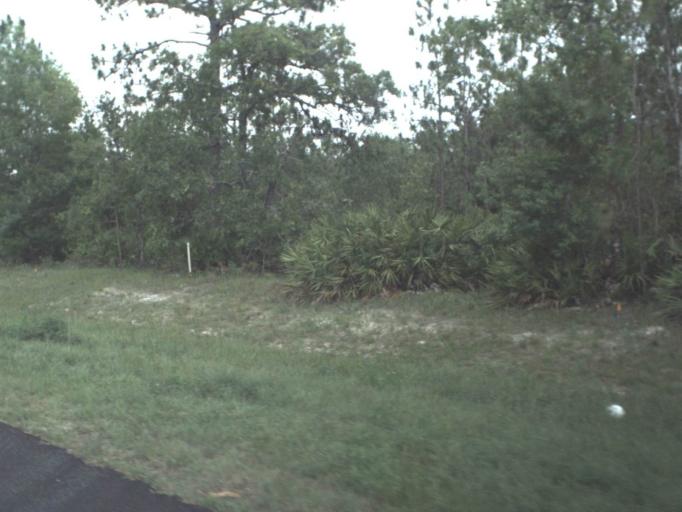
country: US
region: Florida
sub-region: Baker County
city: Macclenny
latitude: 30.1374
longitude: -82.0381
